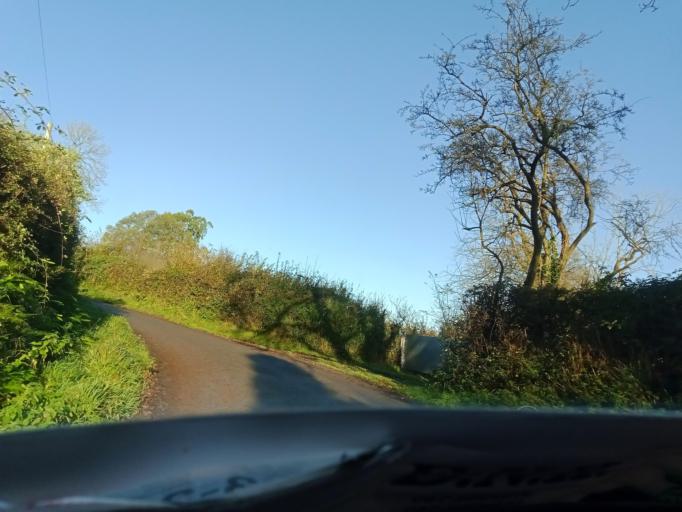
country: IE
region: Leinster
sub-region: Kilkenny
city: Mooncoin
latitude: 52.2919
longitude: -7.1763
